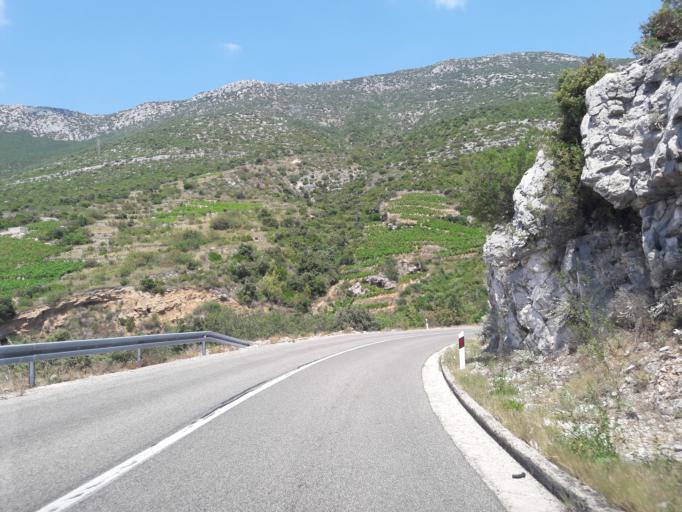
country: HR
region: Dubrovacko-Neretvanska
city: Orebic
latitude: 42.9728
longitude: 17.2406
